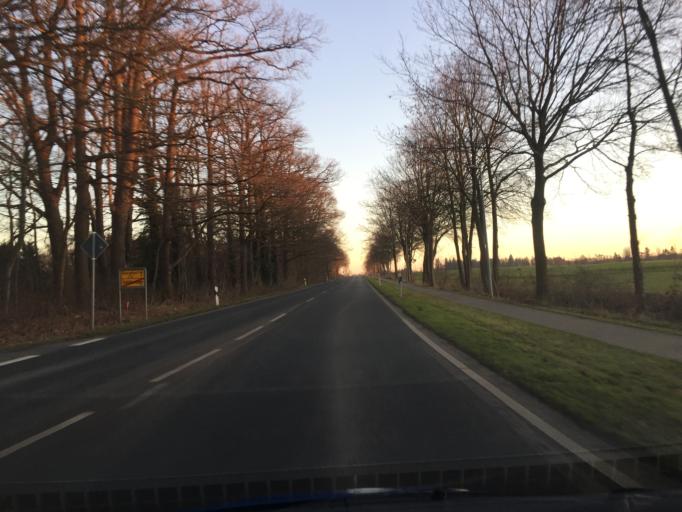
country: DE
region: Lower Saxony
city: Burgdorf
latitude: 52.4662
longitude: 9.9835
